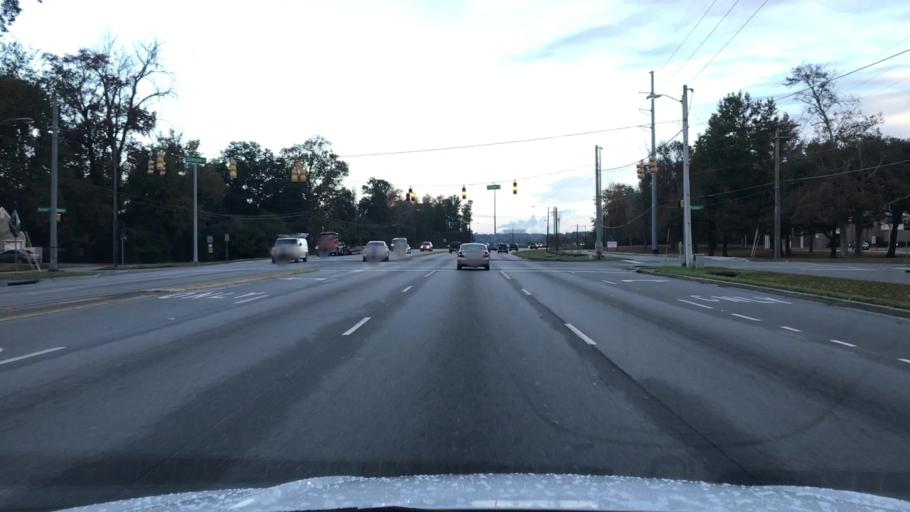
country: US
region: South Carolina
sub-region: Charleston County
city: North Charleston
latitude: 32.8268
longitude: -79.9903
